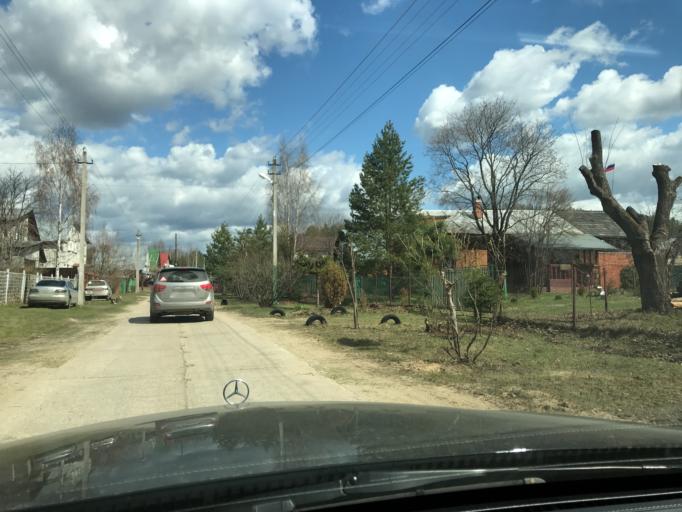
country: RU
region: Vladimir
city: Pokrov
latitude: 55.8567
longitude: 39.2013
